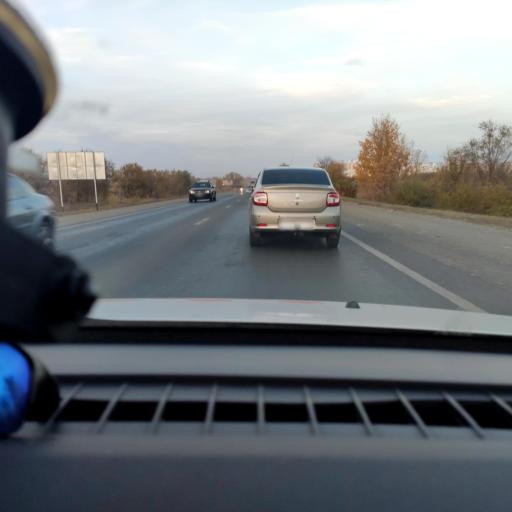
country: RU
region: Samara
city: Samara
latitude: 53.0874
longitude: 50.1449
